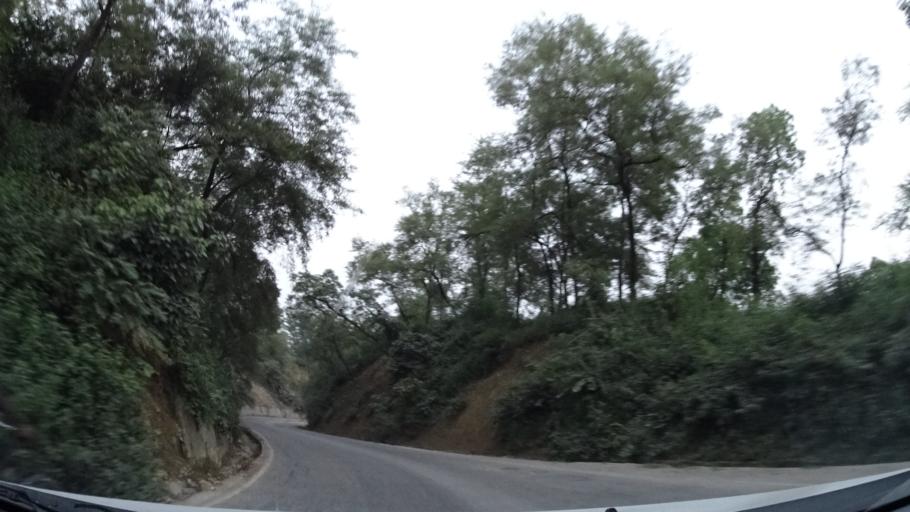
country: IN
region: Uttar Pradesh
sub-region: Maharajganj
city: Nichlaul
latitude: 27.5531
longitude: 83.8016
